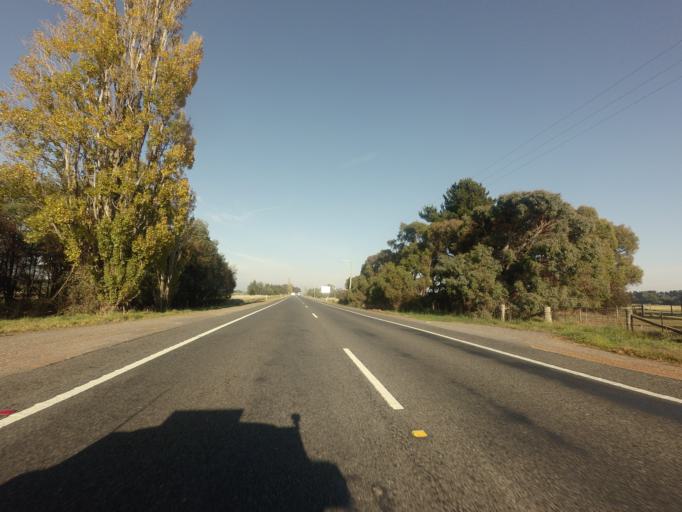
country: AU
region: Tasmania
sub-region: Northern Midlands
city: Longford
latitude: -41.5786
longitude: 147.1377
